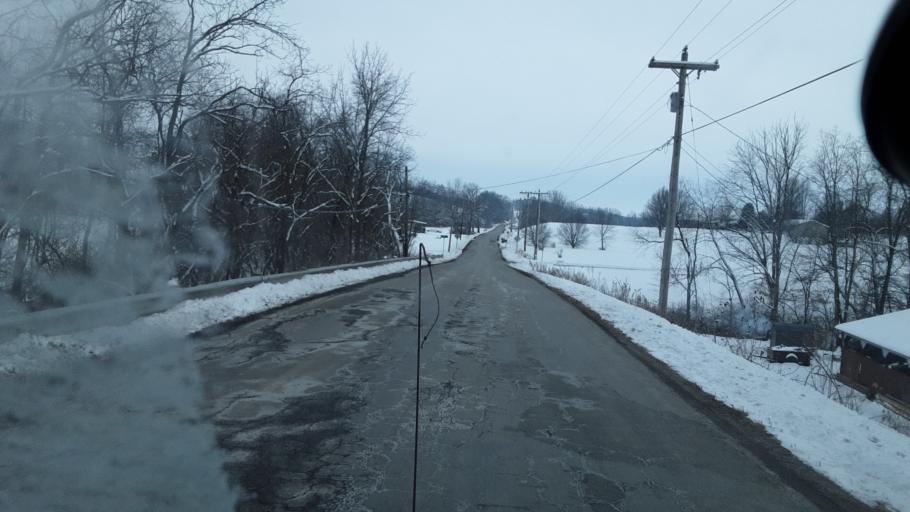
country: US
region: Ohio
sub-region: Perry County
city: Thornport
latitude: 39.9545
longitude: -82.3364
